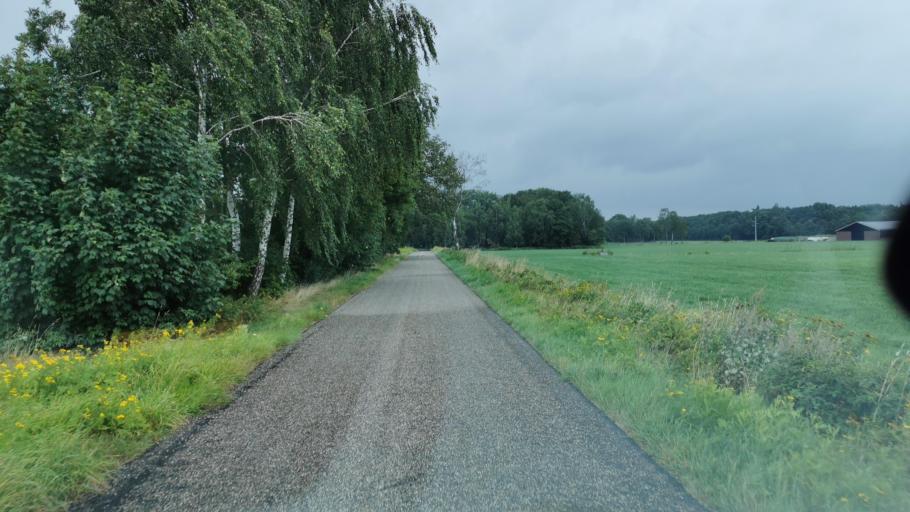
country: NL
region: Overijssel
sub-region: Gemeente Losser
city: Losser
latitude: 52.2370
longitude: 6.9900
